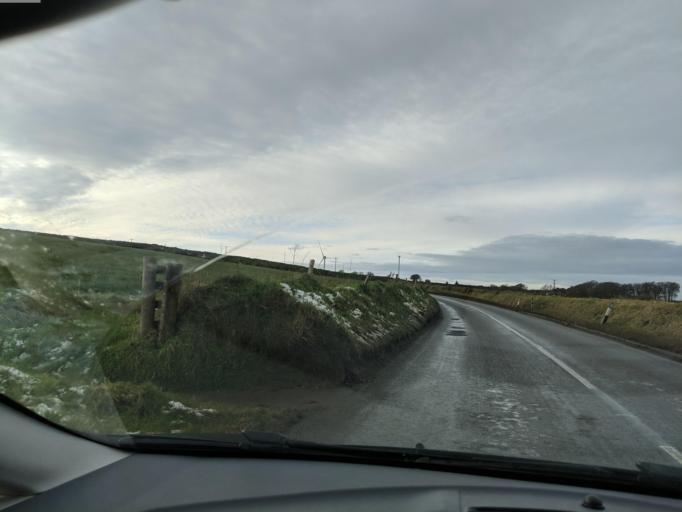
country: GB
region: England
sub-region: Cornwall
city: Jacobstow
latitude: 50.6641
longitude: -4.5850
